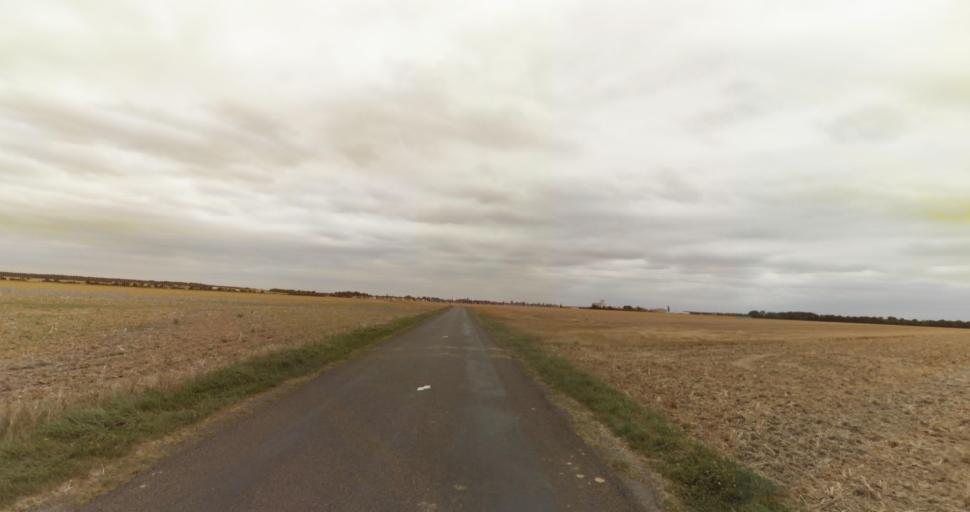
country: FR
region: Haute-Normandie
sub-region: Departement de l'Eure
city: Marcilly-sur-Eure
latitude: 48.9249
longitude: 1.2716
